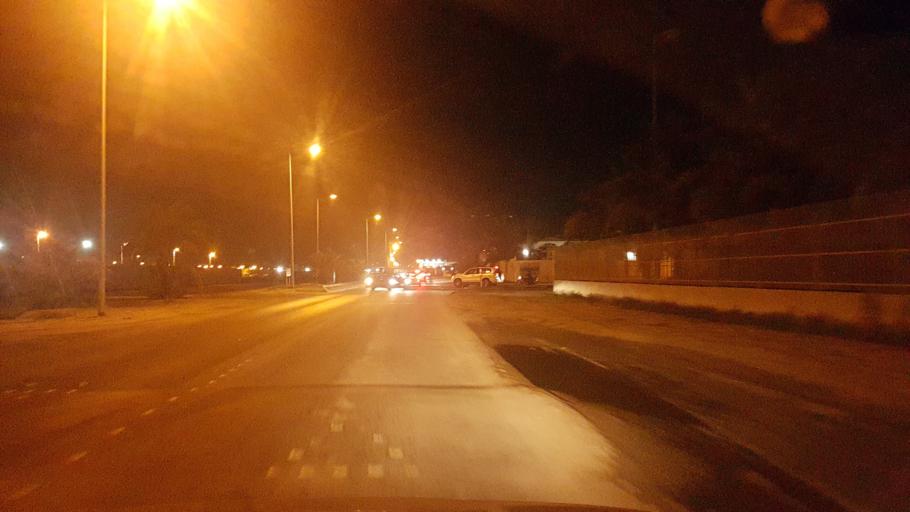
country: BH
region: Muharraq
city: Al Hadd
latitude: 26.2755
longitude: 50.6399
